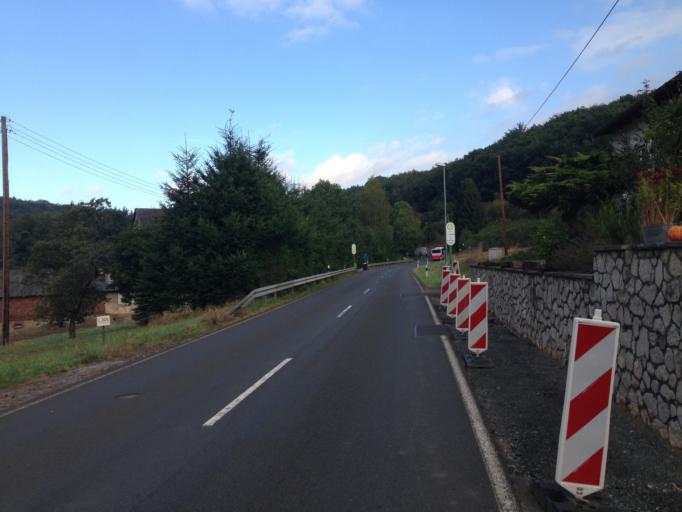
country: DE
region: Hesse
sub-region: Regierungsbezirk Giessen
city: Heuchelheim
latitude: 50.6325
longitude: 8.5732
